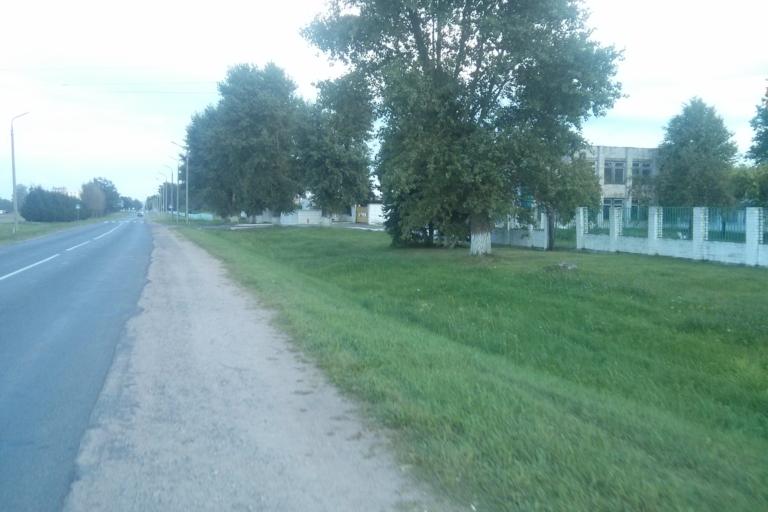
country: BY
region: Minsk
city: Chervyen'
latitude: 53.7214
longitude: 28.3887
